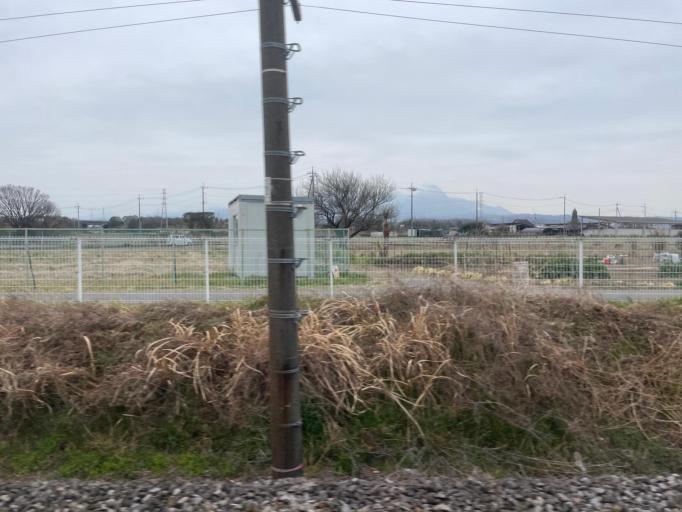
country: JP
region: Gunma
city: Shibukawa
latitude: 36.4524
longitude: 139.0203
